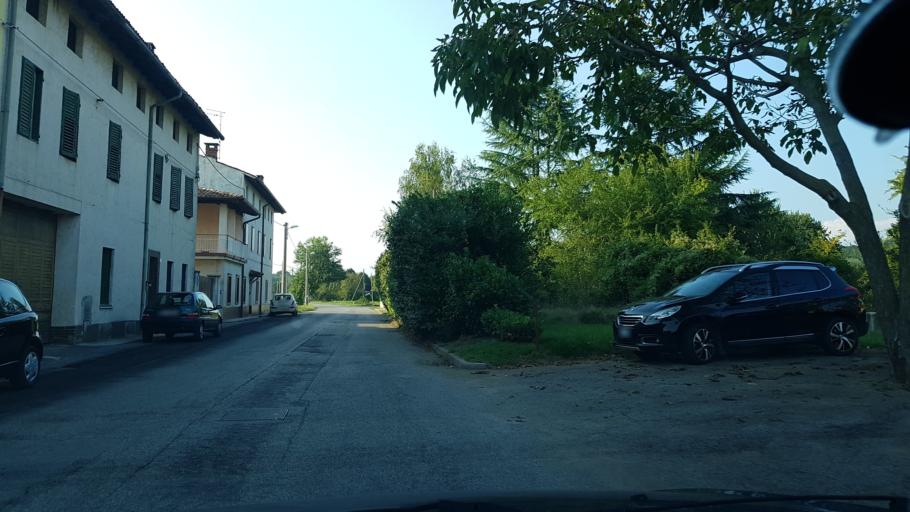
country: IT
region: Friuli Venezia Giulia
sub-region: Provincia di Gorizia
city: Mossa
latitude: 45.9408
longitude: 13.5752
